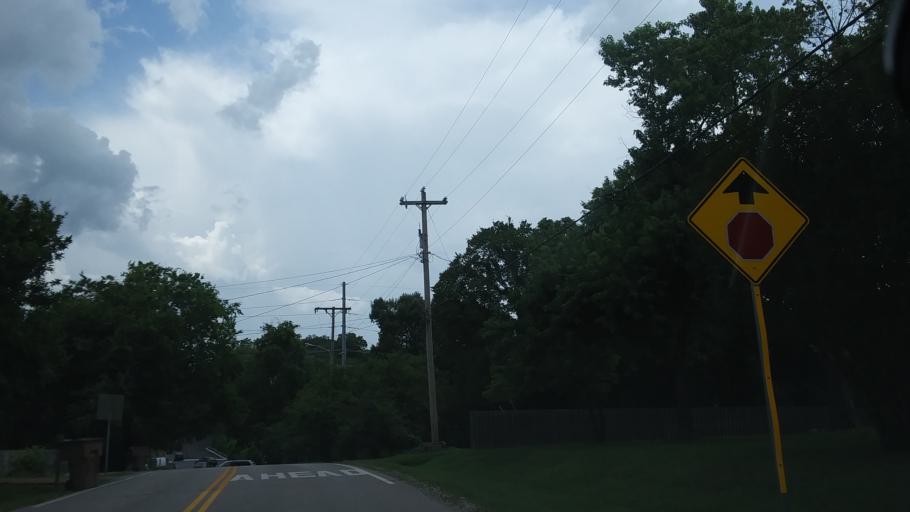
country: US
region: Tennessee
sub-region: Davidson County
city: Belle Meade
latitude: 36.1395
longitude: -86.8785
